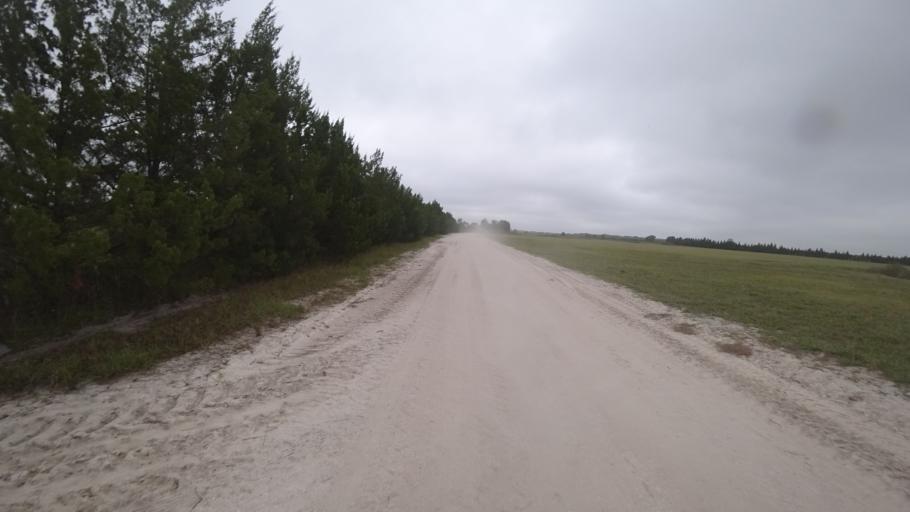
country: US
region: Florida
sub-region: Sarasota County
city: Warm Mineral Springs
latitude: 27.2979
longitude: -82.1345
